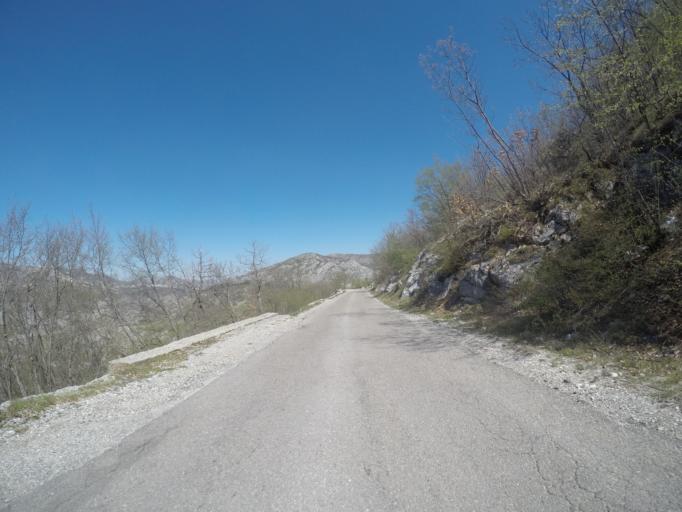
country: ME
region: Cetinje
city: Cetinje
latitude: 42.4491
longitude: 18.8733
